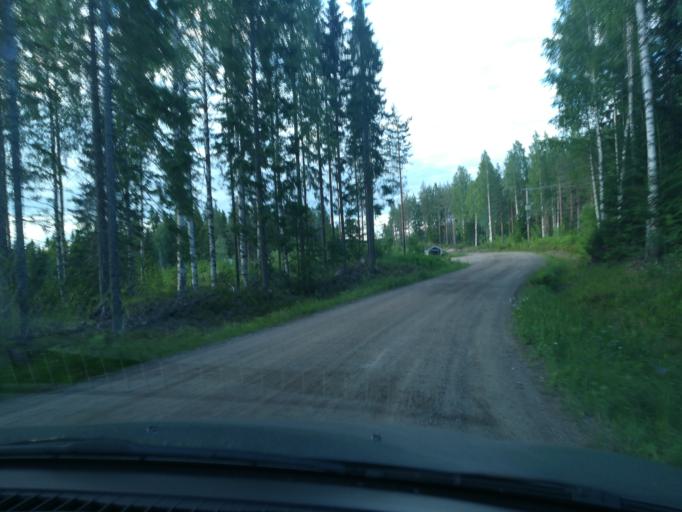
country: FI
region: Southern Savonia
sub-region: Mikkeli
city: Puumala
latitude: 61.6136
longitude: 28.1448
